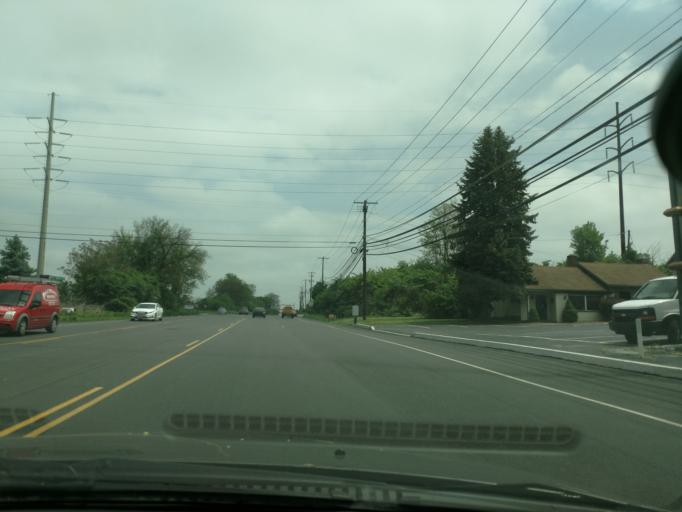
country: US
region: Pennsylvania
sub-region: Berks County
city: Wernersville
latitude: 40.3267
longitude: -76.0537
